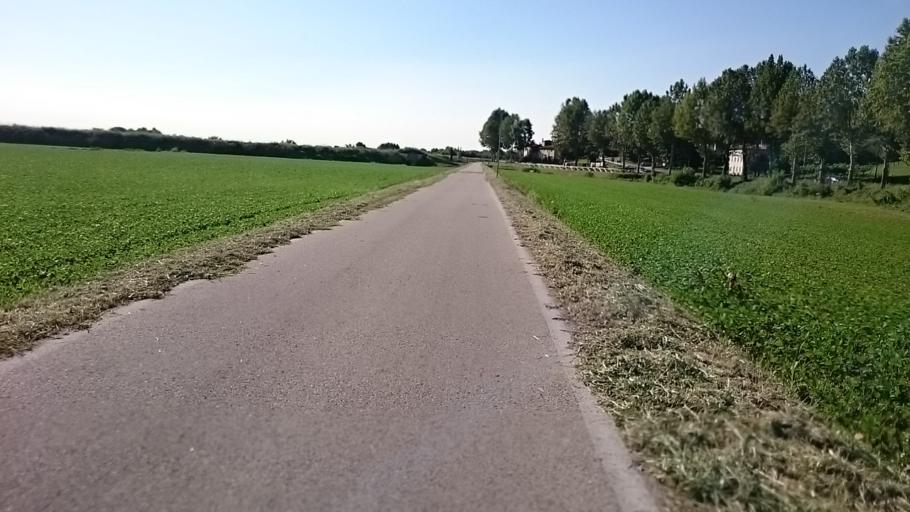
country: IT
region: Veneto
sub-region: Provincia di Vicenza
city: Longare
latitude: 45.4897
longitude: 11.5974
